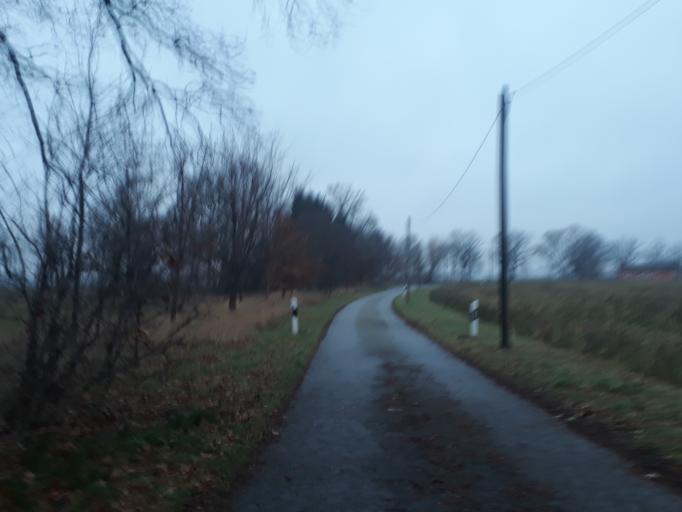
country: DE
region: Saxony
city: Guttau
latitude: 51.2627
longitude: 14.5582
